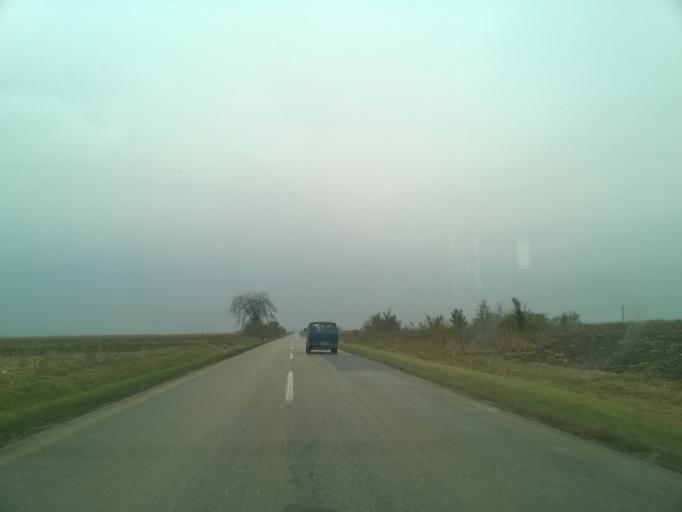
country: RS
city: Crepaja
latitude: 45.0358
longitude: 20.6386
